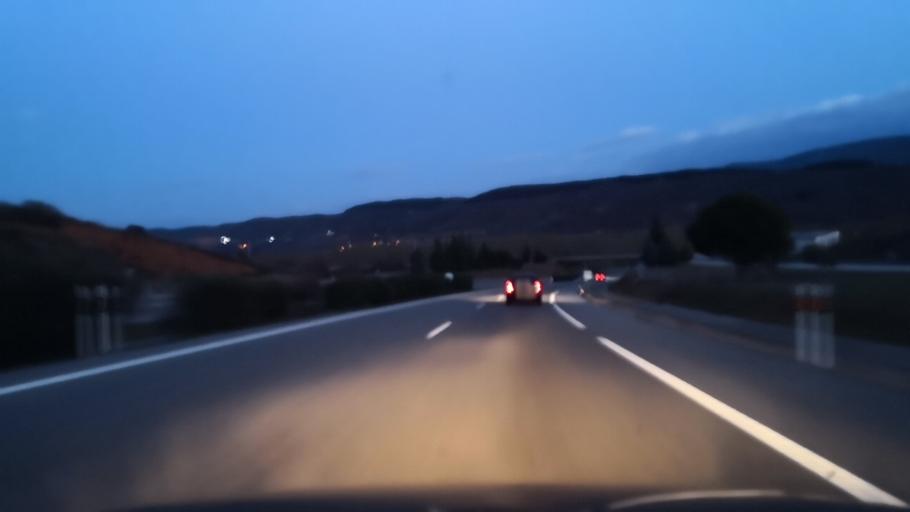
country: ES
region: Castille and Leon
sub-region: Provincia de Leon
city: Torre del Bierzo
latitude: 42.6114
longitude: -6.3908
